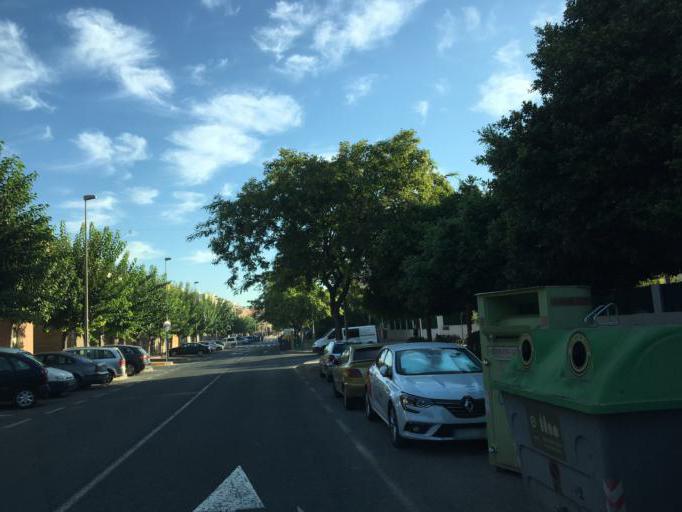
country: ES
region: Murcia
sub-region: Murcia
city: Murcia
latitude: 38.0145
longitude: -1.1501
